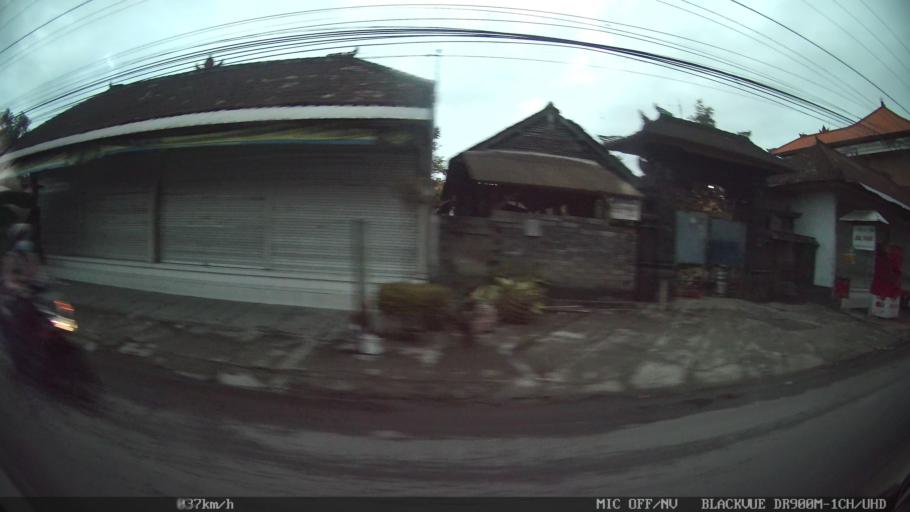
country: ID
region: Bali
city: Banjar Pasekan
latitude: -8.6129
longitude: 115.2836
